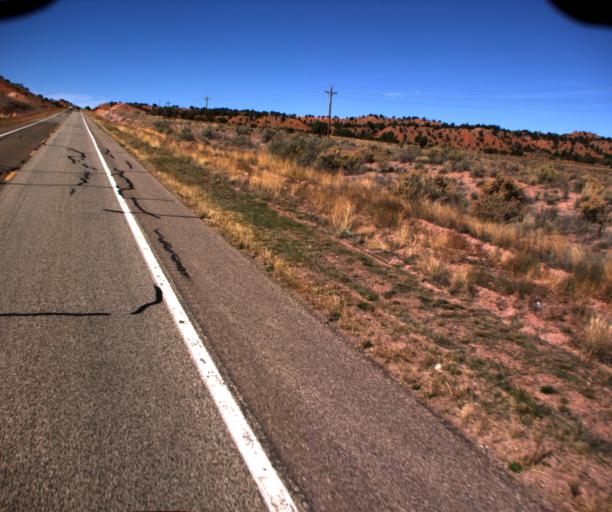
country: US
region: Arizona
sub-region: Mohave County
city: Colorado City
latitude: 36.8786
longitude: -112.8856
